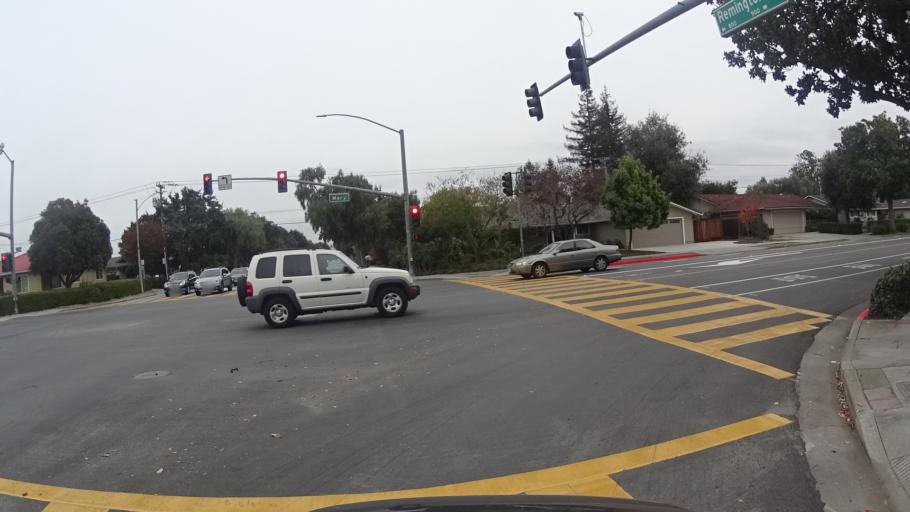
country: US
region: California
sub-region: Santa Clara County
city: Sunnyvale
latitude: 37.3594
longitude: -122.0504
